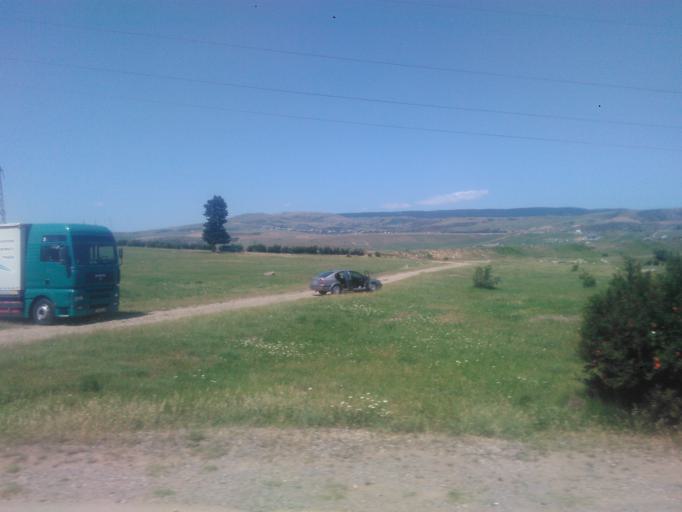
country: GE
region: T'bilisi
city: Tbilisi
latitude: 41.7134
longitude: 44.8821
